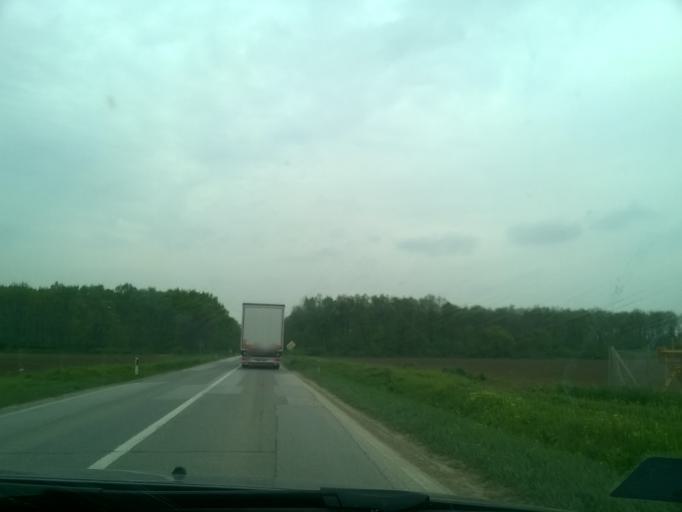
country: RS
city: Jarak
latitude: 44.9056
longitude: 19.7646
